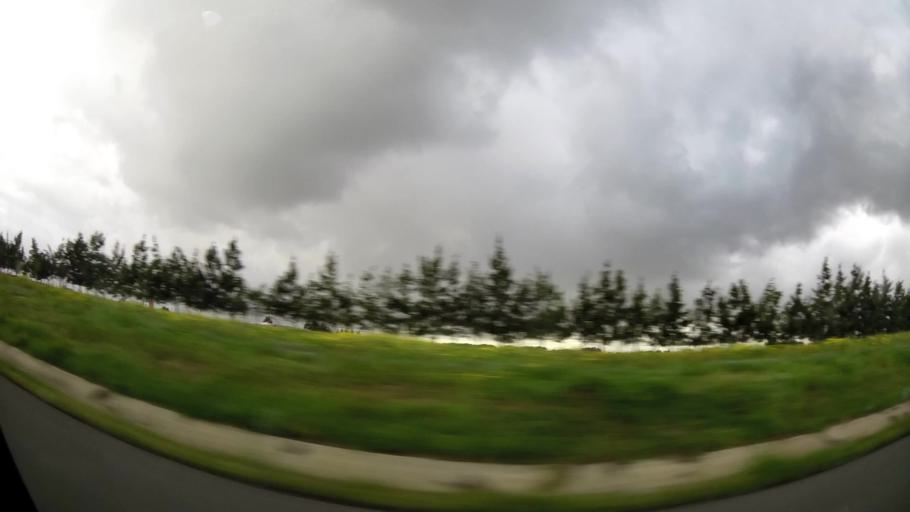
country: MA
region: Grand Casablanca
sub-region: Mediouna
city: Tit Mellil
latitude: 33.5740
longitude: -7.4559
